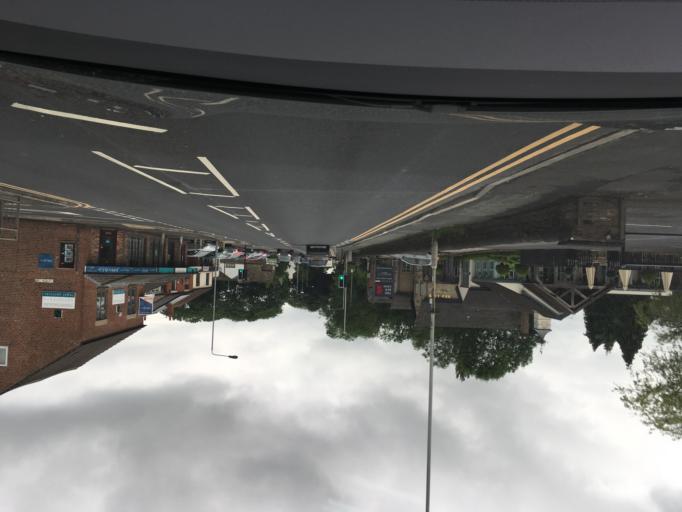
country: GB
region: England
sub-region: Cheshire East
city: Disley
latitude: 53.3640
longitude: -2.0673
